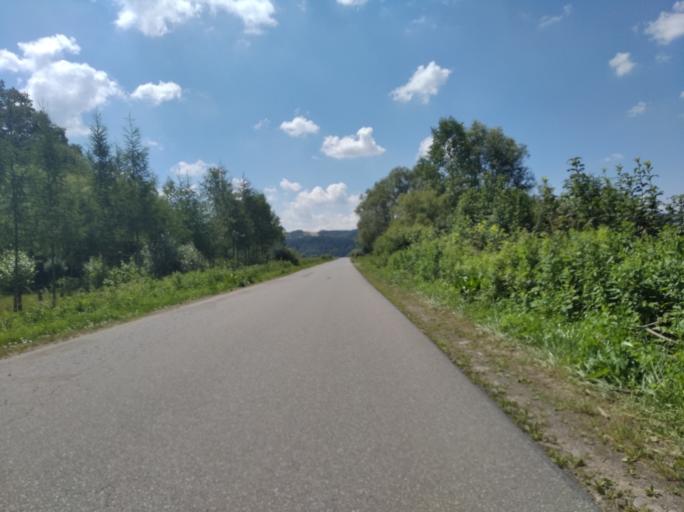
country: PL
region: Subcarpathian Voivodeship
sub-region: Powiat brzozowski
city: Dydnia
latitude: 49.7054
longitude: 22.2093
